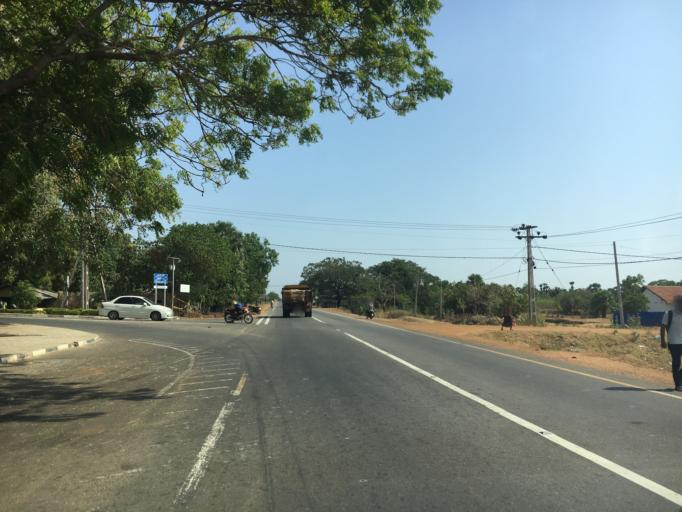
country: LK
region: Northern Province
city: Kilinochchi
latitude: 9.4377
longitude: 80.4076
